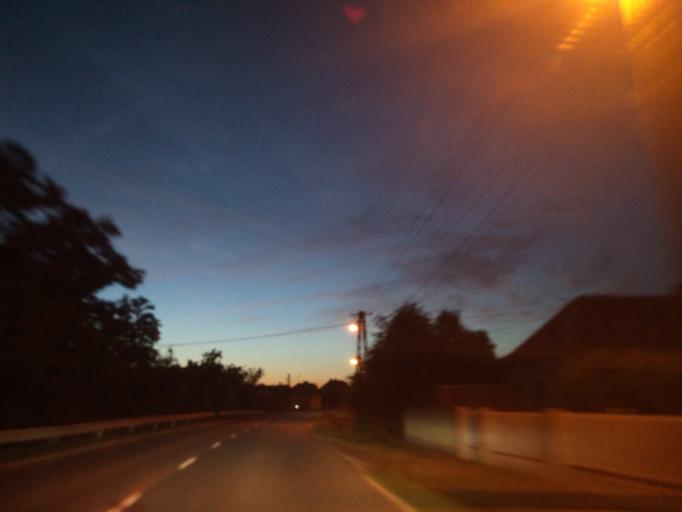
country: HU
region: Vas
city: Vasvar
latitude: 47.0408
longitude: 16.8081
